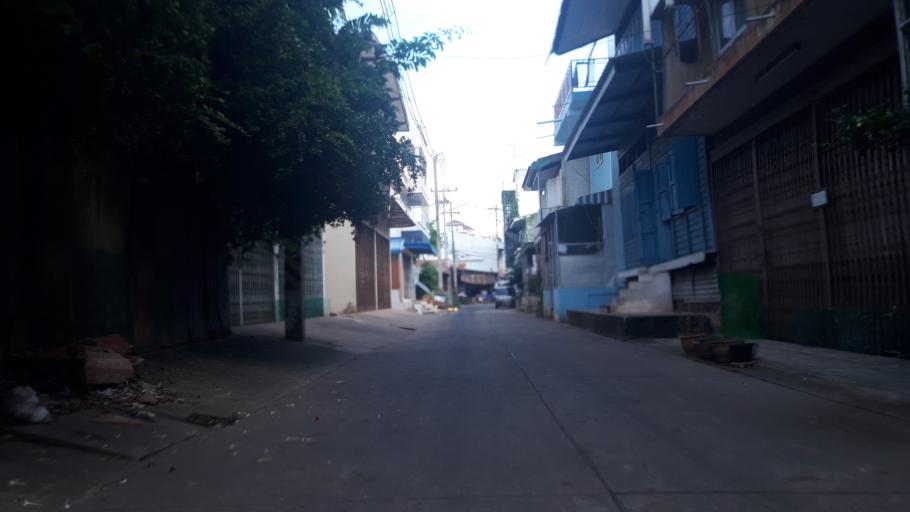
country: TH
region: Phichit
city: Thap Khlo
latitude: 16.1681
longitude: 100.5789
